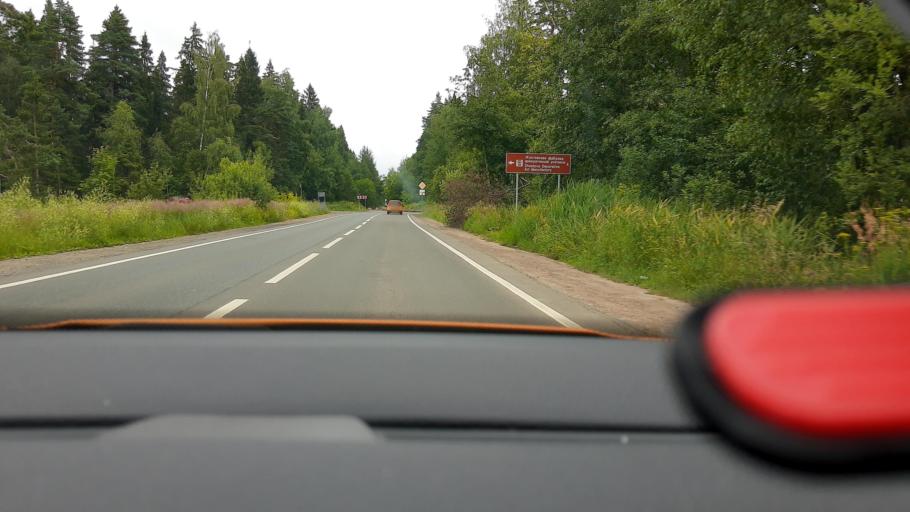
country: RU
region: Moskovskaya
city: Pirogovskiy
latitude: 55.9996
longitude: 37.6802
